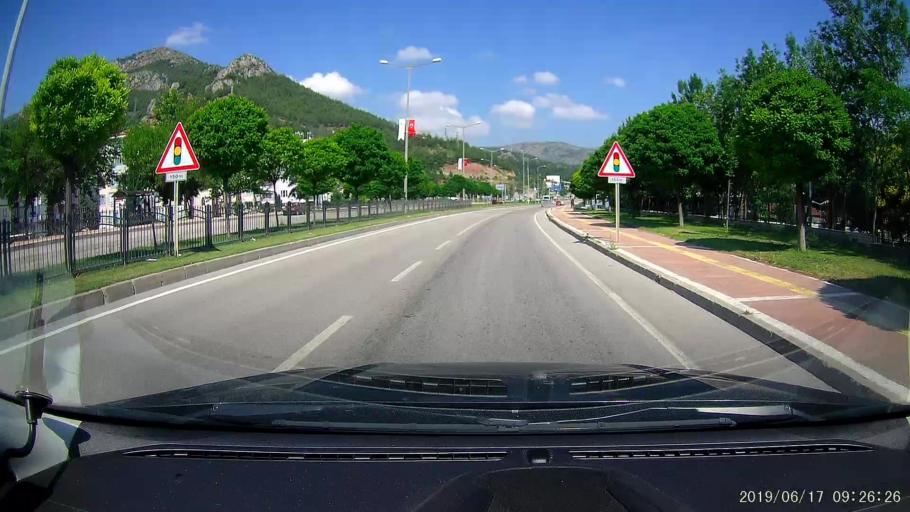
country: TR
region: Amasya
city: Amasya
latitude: 40.6695
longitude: 35.8357
